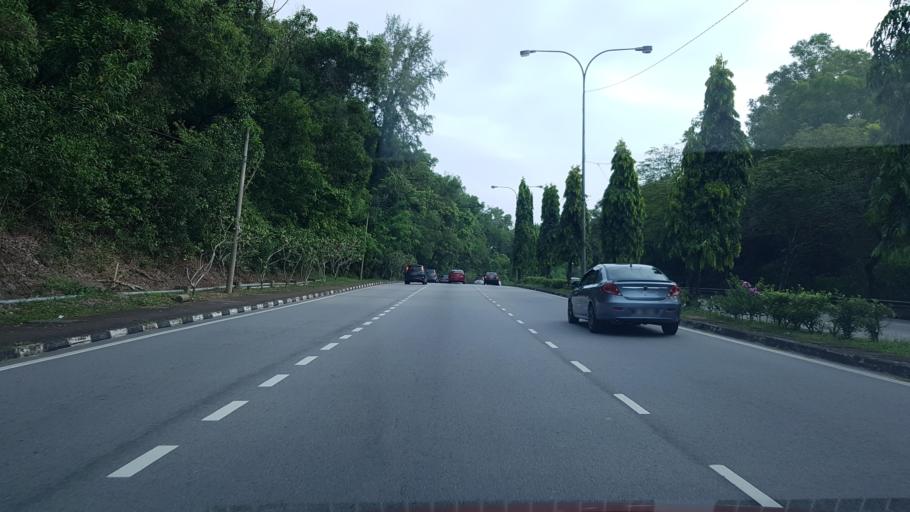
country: MY
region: Terengganu
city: Kuala Terengganu
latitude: 5.3220
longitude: 103.1365
